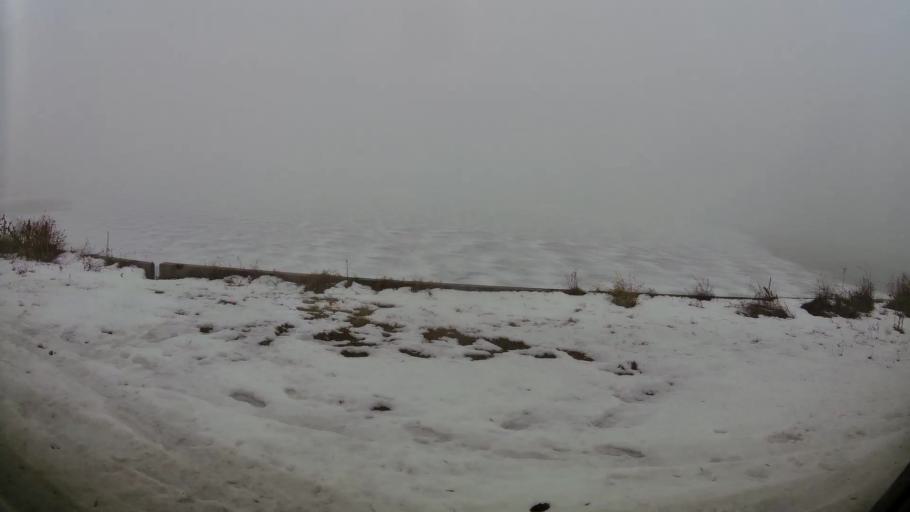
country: RO
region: Ilfov
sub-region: Comuna Chiajna
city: Rosu
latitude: 44.4506
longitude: 26.0258
